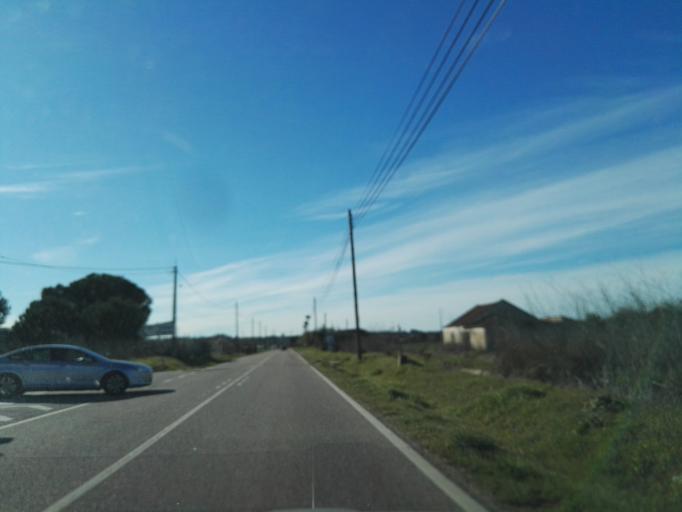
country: PT
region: Portalegre
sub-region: Gaviao
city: Gaviao
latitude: 39.4613
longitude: -8.0266
